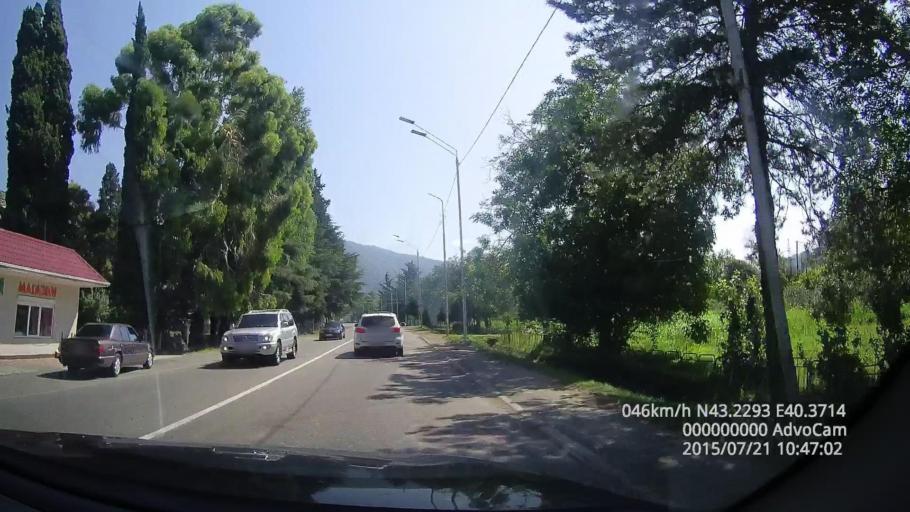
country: GE
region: Abkhazia
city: Bich'vinta
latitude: 43.2293
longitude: 40.3716
